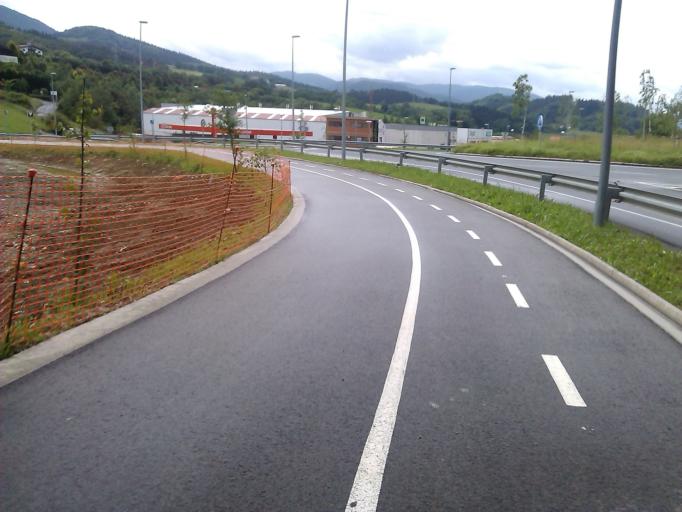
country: ES
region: Basque Country
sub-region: Provincia de Guipuzcoa
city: Urnieta
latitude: 43.2332
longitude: -1.9999
